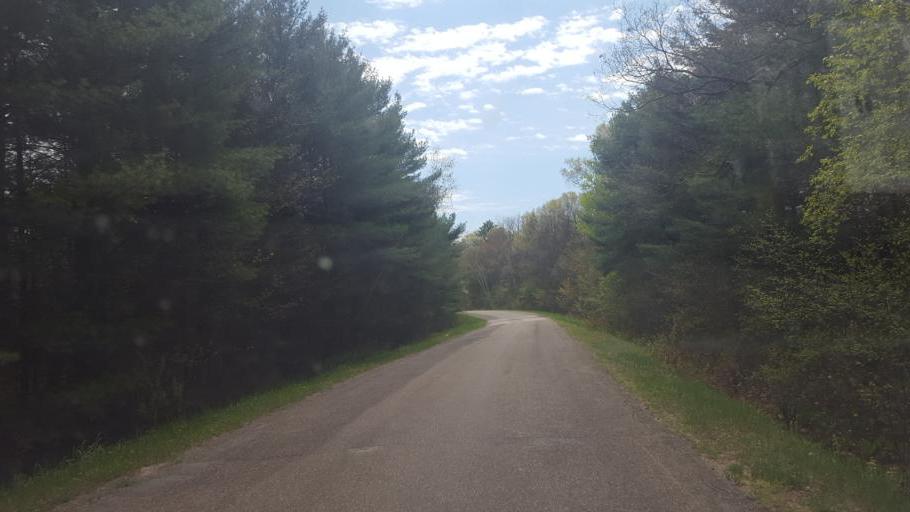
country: US
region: Wisconsin
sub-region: Clark County
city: Neillsville
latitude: 44.2774
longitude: -90.4994
